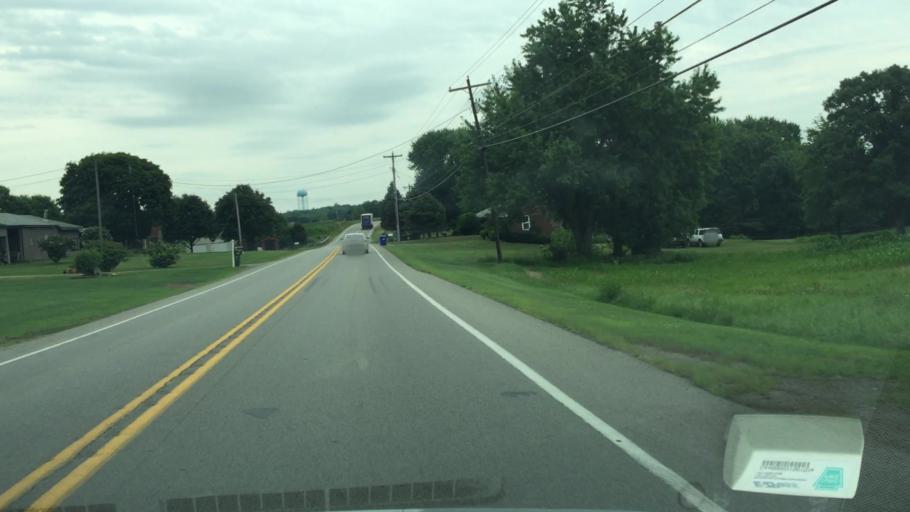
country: US
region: Pennsylvania
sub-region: Butler County
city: Saxonburg
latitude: 40.7236
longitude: -79.8645
